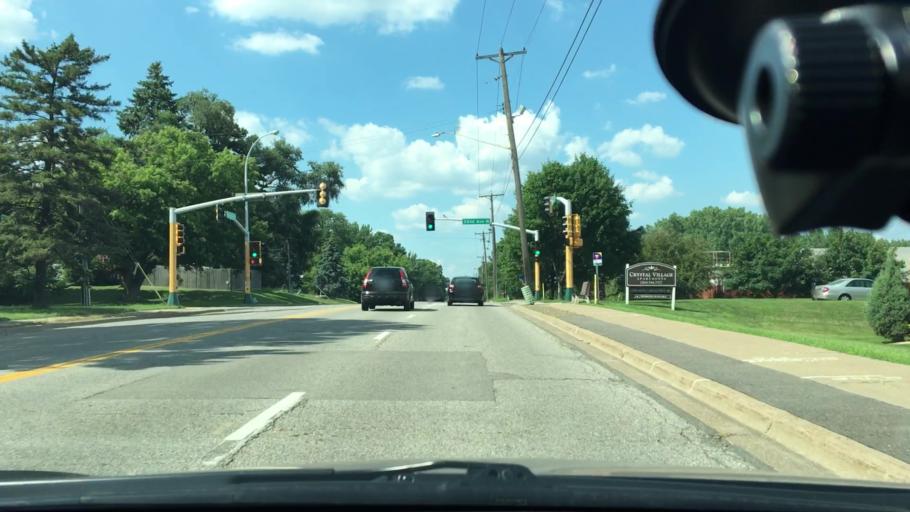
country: US
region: Minnesota
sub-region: Hennepin County
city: New Hope
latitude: 45.0142
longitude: -93.3802
